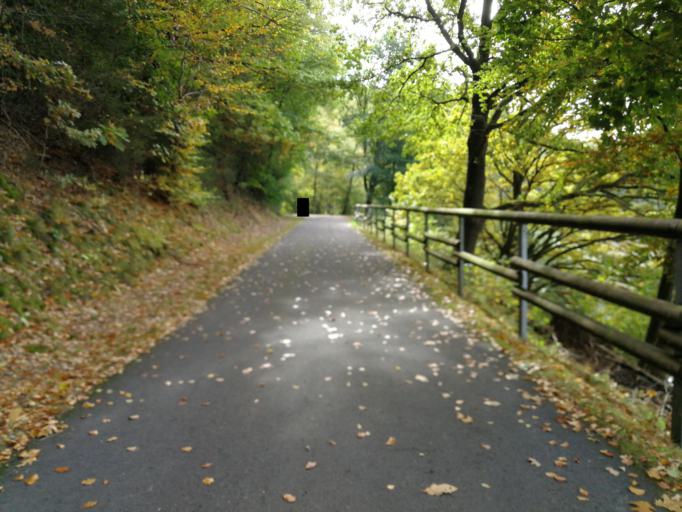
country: DE
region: North Rhine-Westphalia
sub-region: Regierungsbezirk Arnsberg
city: Meschede
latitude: 51.3282
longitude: 8.2661
